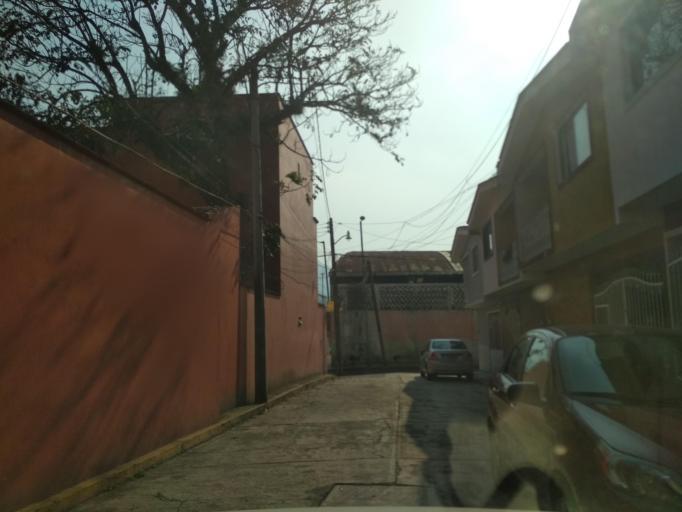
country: MX
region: Veracruz
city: Orizaba
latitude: 18.8569
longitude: -97.0913
